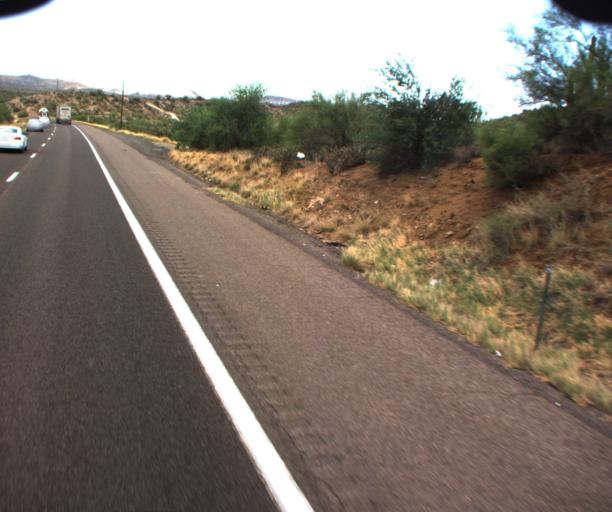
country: US
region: Arizona
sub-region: Yavapai County
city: Black Canyon City
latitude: 34.0236
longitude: -112.1481
